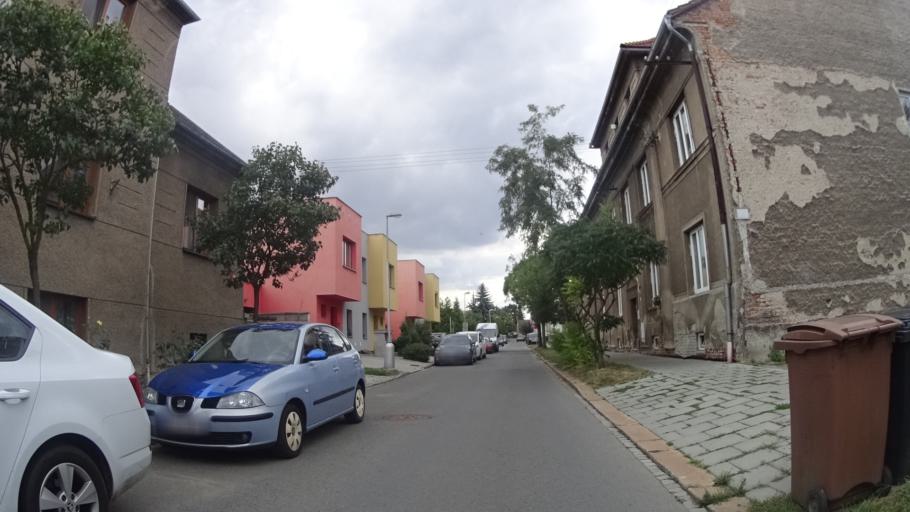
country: CZ
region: Olomoucky
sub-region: Okres Olomouc
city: Olomouc
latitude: 49.6089
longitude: 17.2316
